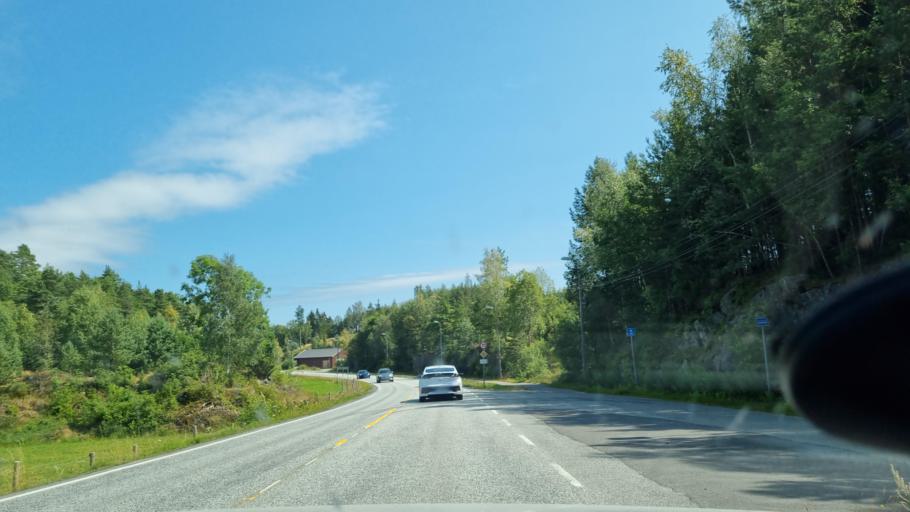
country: NO
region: Aust-Agder
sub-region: Arendal
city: Arendal
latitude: 58.4680
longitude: 8.8482
